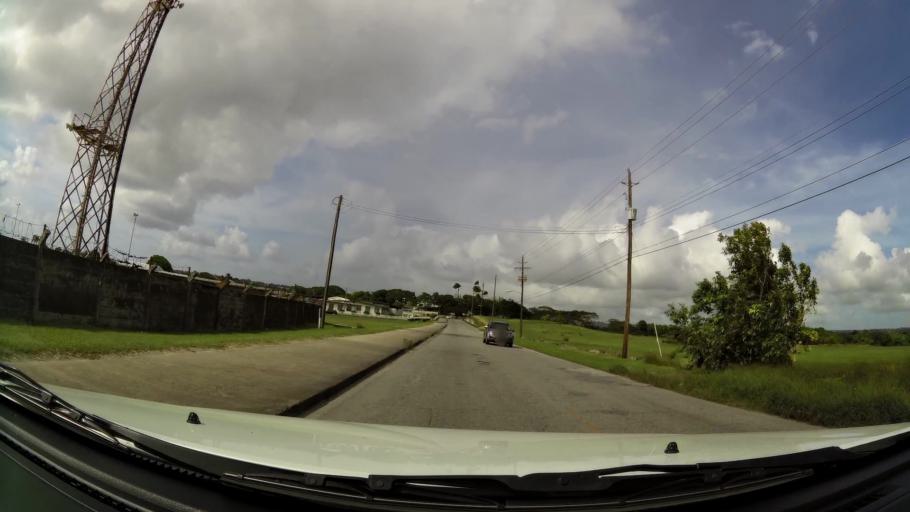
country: BB
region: Saint Michael
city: Bridgetown
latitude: 13.1208
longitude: -59.6038
